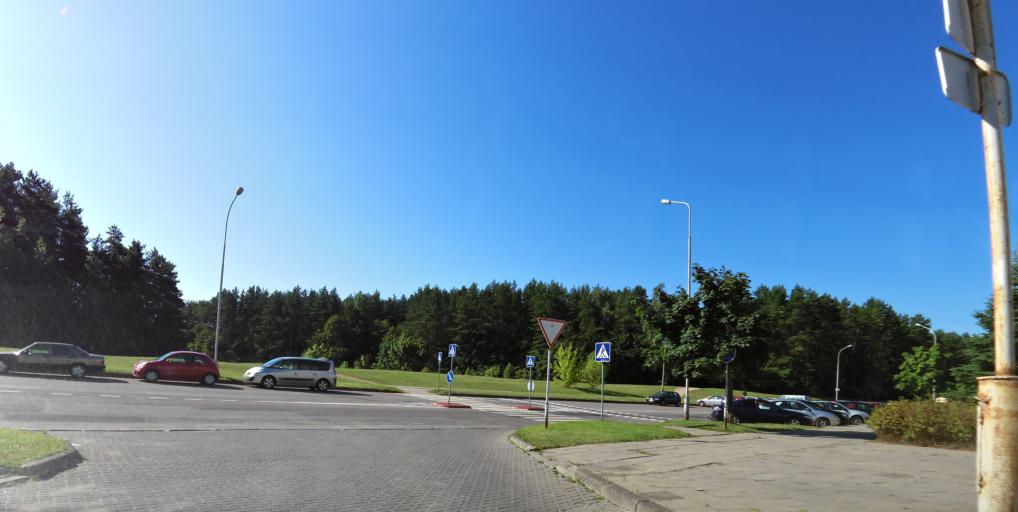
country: LT
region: Vilnius County
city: Pilaite
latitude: 54.7025
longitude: 25.1865
